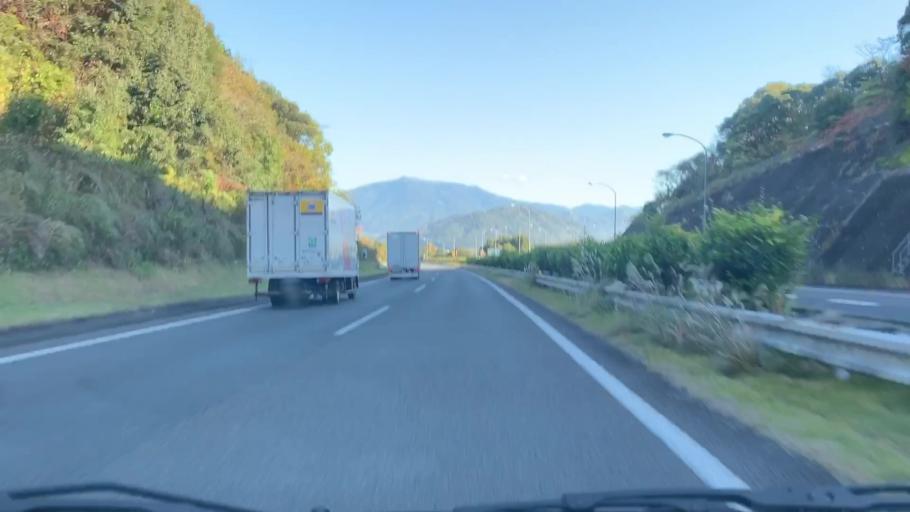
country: JP
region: Saga Prefecture
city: Takeocho-takeo
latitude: 33.2510
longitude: 130.0767
